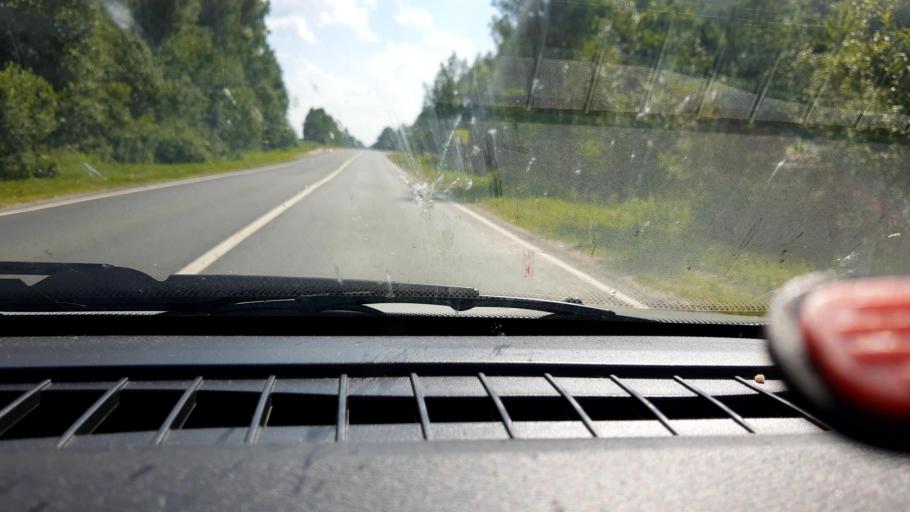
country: RU
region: Nizjnij Novgorod
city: Uren'
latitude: 57.2770
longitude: 45.6336
